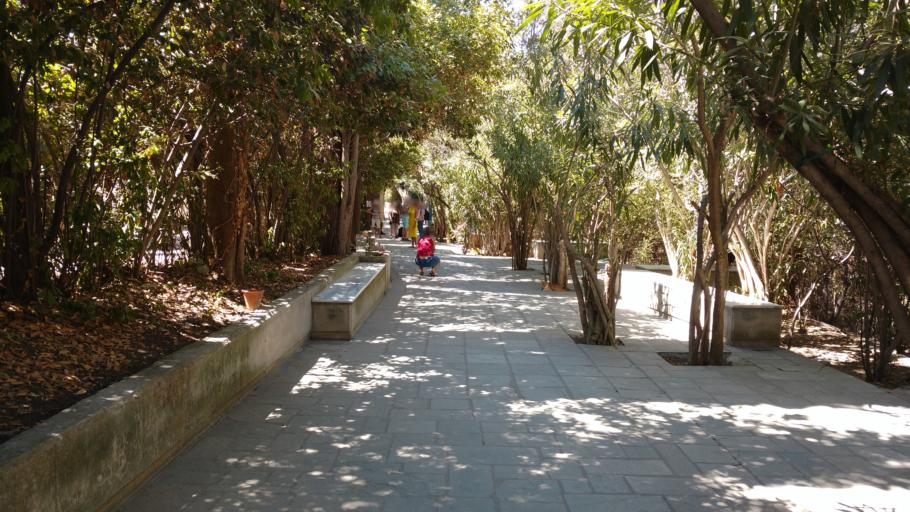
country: GR
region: South Aegean
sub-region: Nomos Dodekanisou
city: Kos
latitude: 36.8764
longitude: 27.2589
